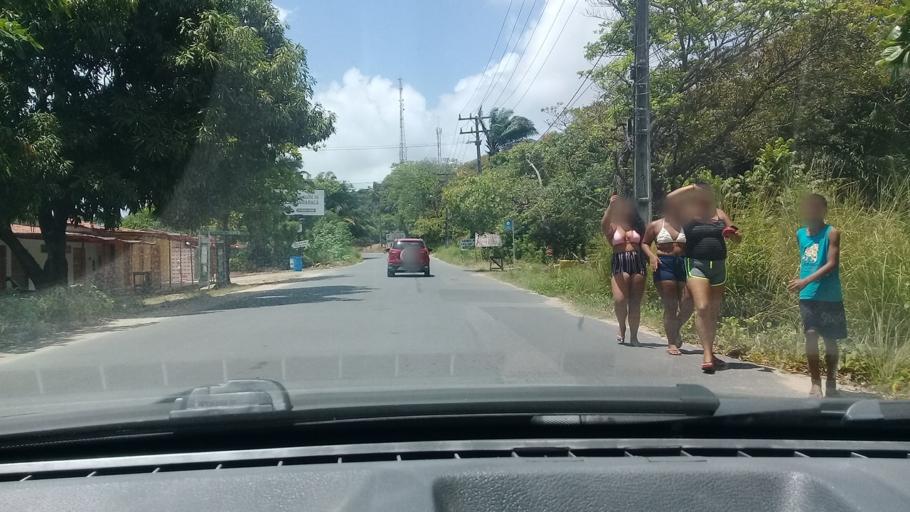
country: BR
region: Pernambuco
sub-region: Itamaraca
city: Itamaraca
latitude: -7.7727
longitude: -34.8365
